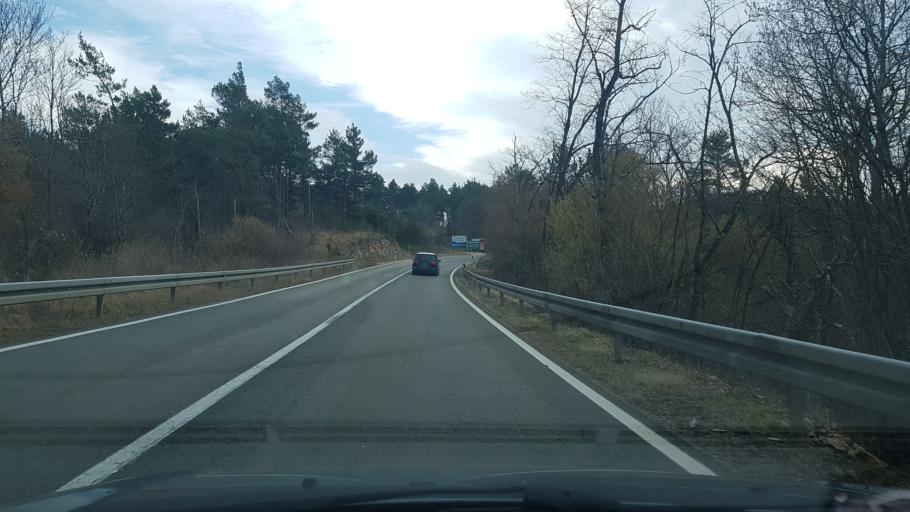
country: SI
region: Ilirska Bistrica
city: Ilirska Bistrica
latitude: 45.4792
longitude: 14.2618
